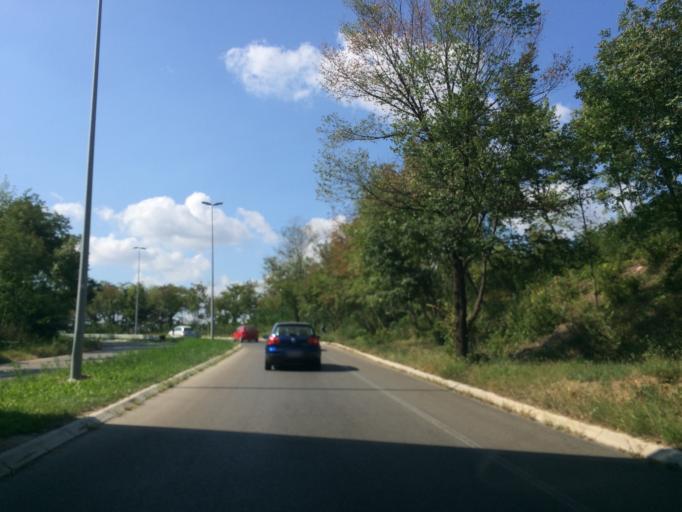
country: RS
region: Autonomna Pokrajina Vojvodina
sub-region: Juznobacki Okrug
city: Novi Sad
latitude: 45.2289
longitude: 19.8550
